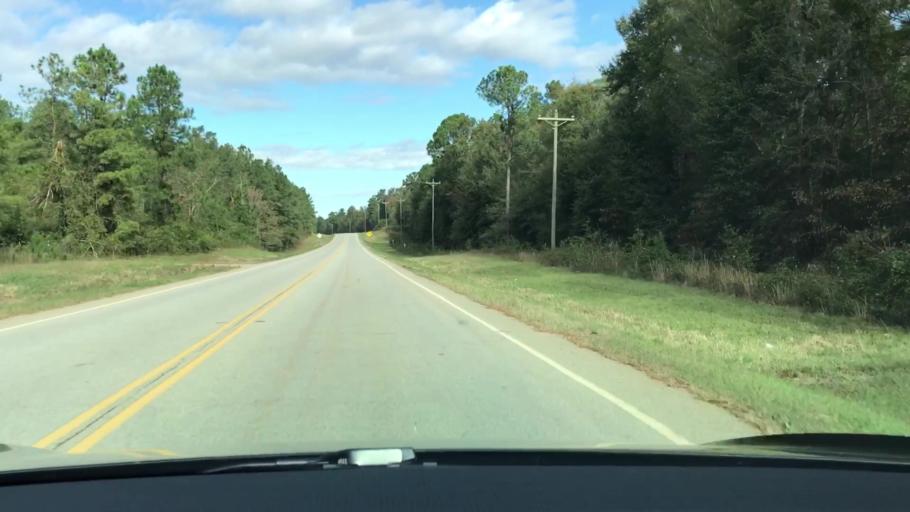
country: US
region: Georgia
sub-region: Jefferson County
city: Louisville
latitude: 33.0848
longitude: -82.4140
